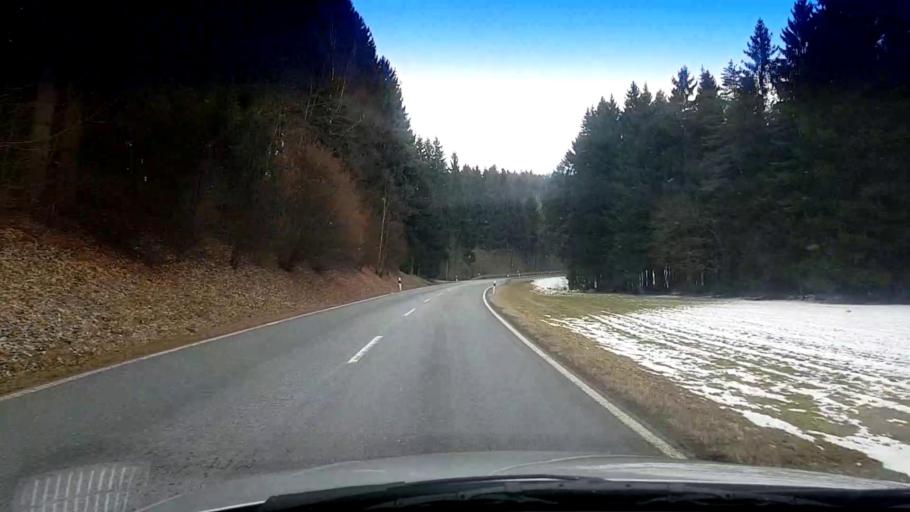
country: DE
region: Bavaria
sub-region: Upper Franconia
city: Marktleugast
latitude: 50.1776
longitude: 11.6563
